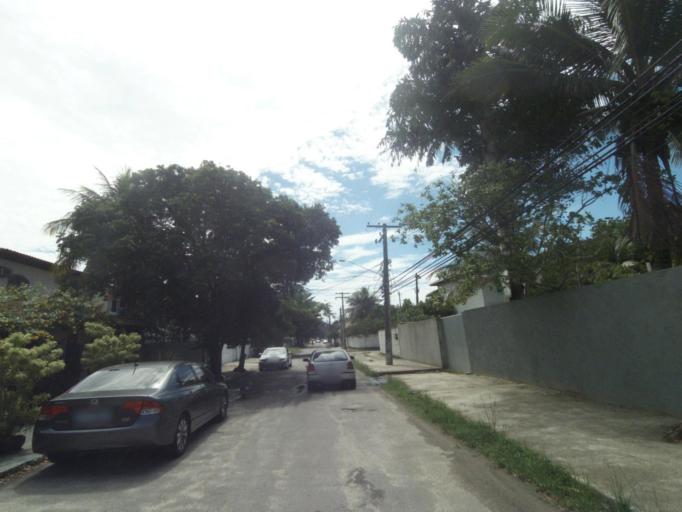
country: BR
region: Rio de Janeiro
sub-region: Niteroi
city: Niteroi
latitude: -22.9446
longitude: -43.0398
